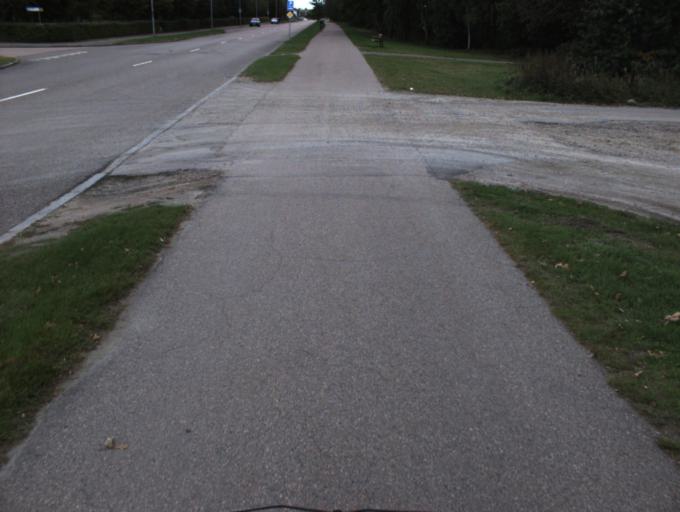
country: SE
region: Skane
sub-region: Helsingborg
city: Helsingborg
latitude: 56.0061
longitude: 12.7265
